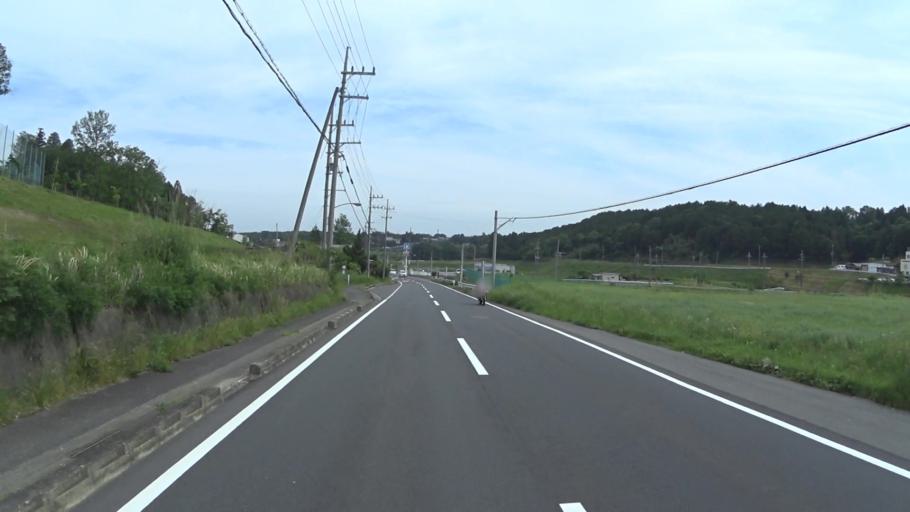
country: JP
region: Shiga Prefecture
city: Kitahama
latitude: 35.1384
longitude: 135.8819
